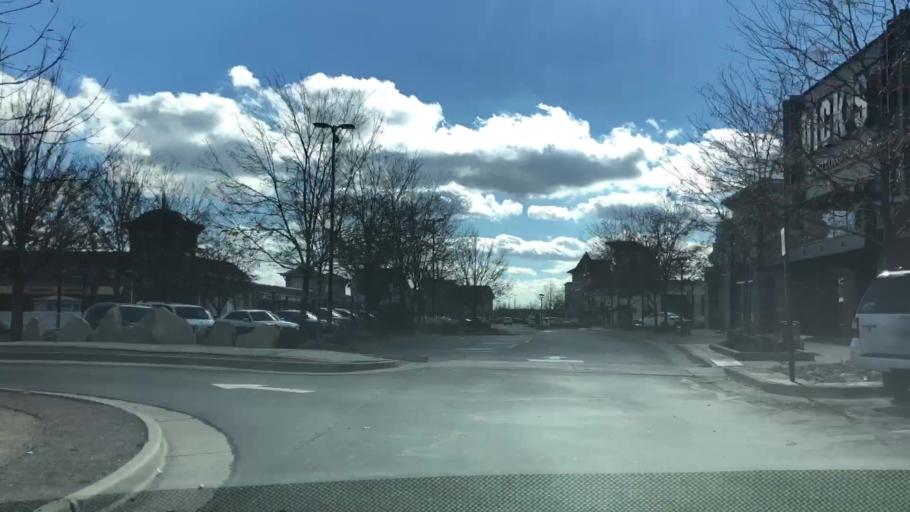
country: US
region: Colorado
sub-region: Larimer County
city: Loveland
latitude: 40.4161
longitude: -104.9898
